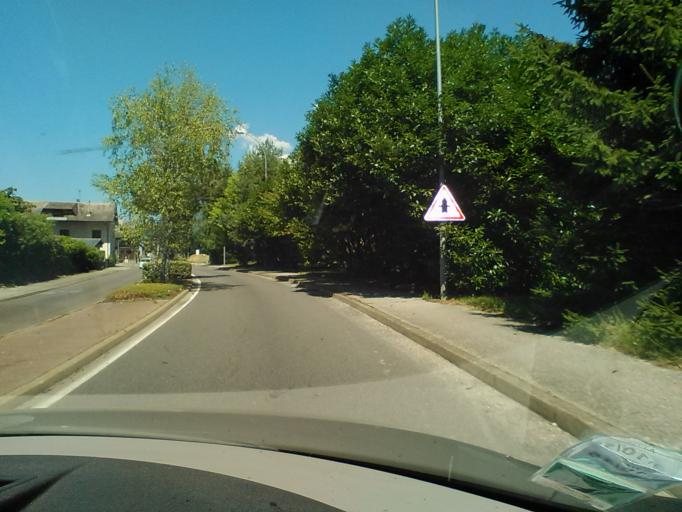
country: FR
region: Rhone-Alpes
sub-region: Departement de la Savoie
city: Challes-les-Eaux
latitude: 45.5351
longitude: 5.9924
